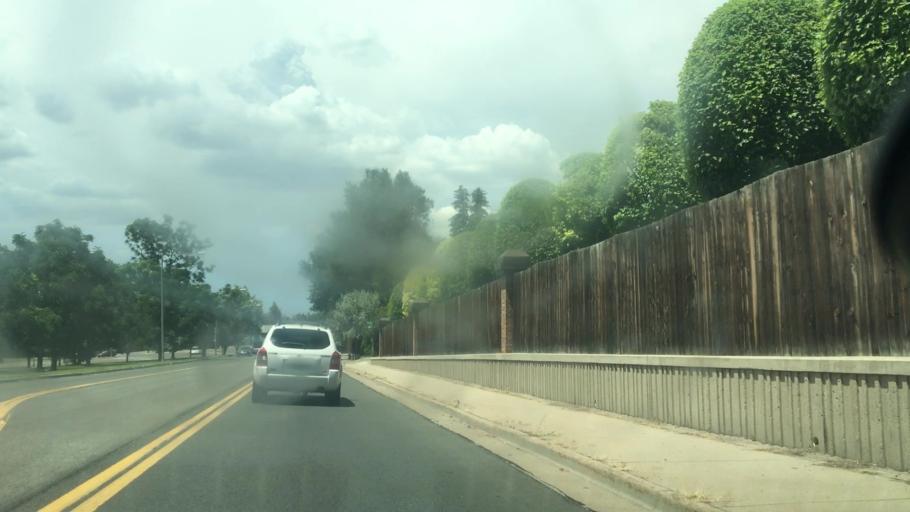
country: US
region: Colorado
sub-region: Arapahoe County
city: Glendale
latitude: 39.7134
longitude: -104.9389
